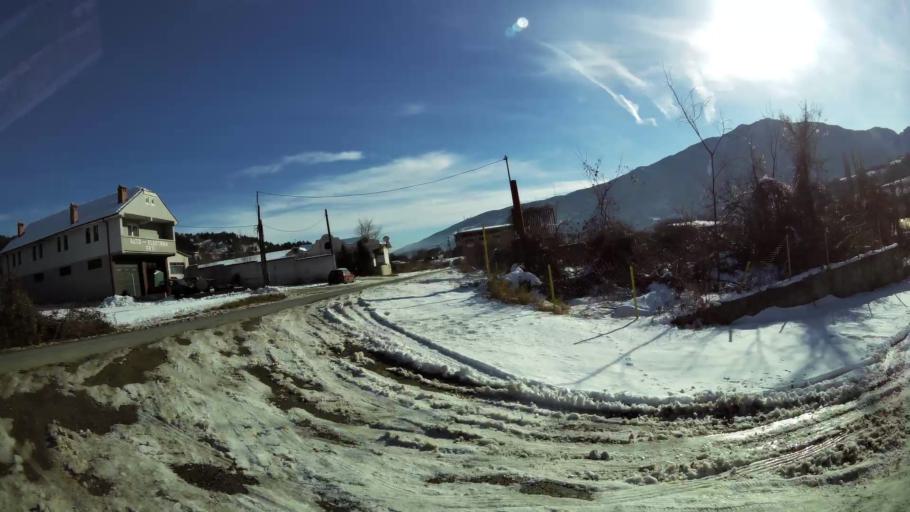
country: MK
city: Ljubin
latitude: 41.9873
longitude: 21.2958
